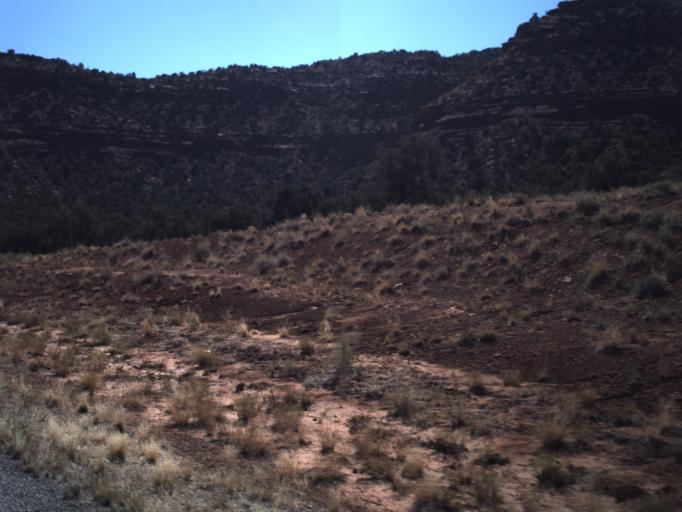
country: US
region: Utah
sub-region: San Juan County
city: Blanding
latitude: 37.6588
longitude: -110.1828
